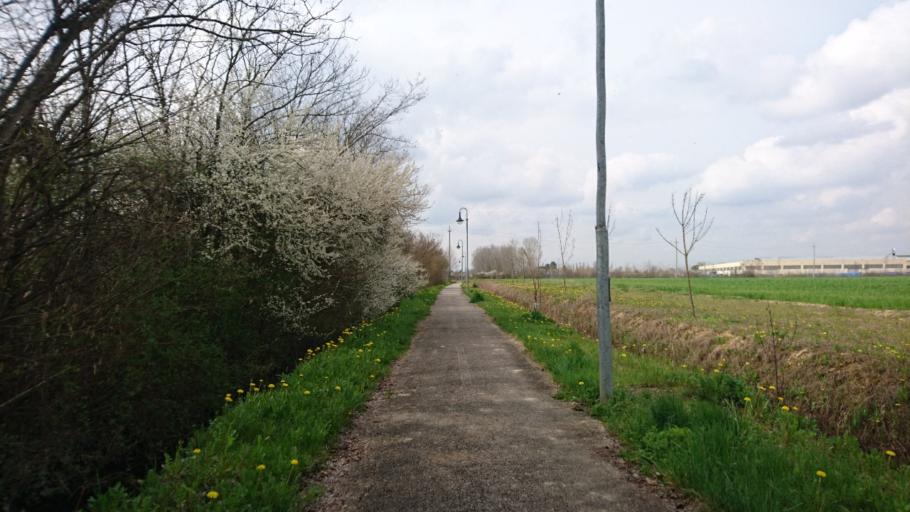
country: IT
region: Veneto
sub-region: Provincia di Padova
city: Limena
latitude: 45.4887
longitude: 11.8272
